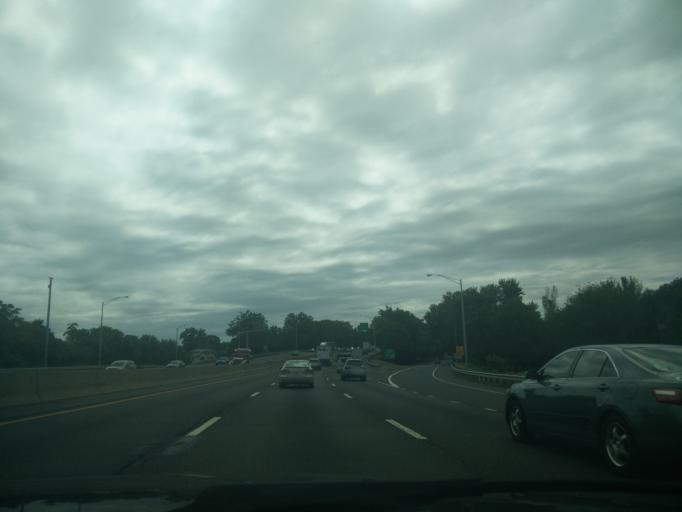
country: US
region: Connecticut
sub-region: Fairfield County
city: Stratford
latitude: 41.1855
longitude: -73.1380
